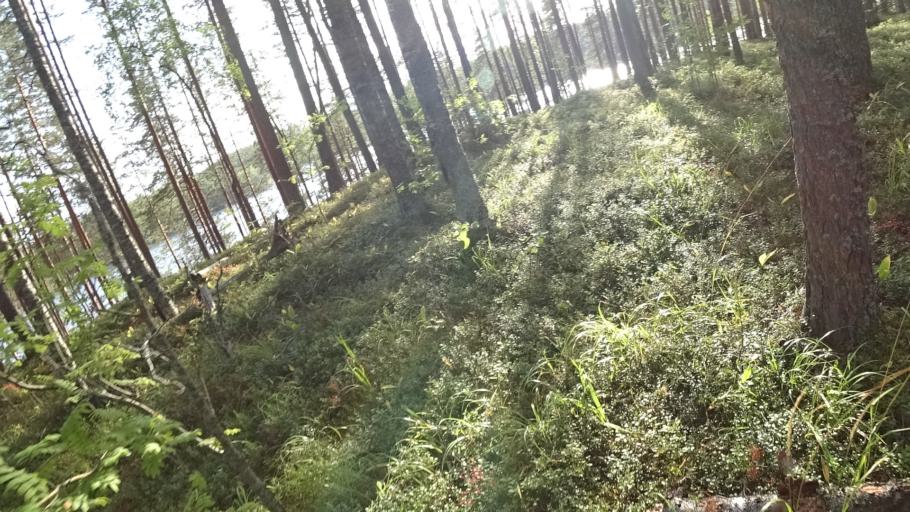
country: FI
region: North Karelia
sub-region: Joensuu
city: Ilomantsi
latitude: 62.5719
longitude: 31.1767
